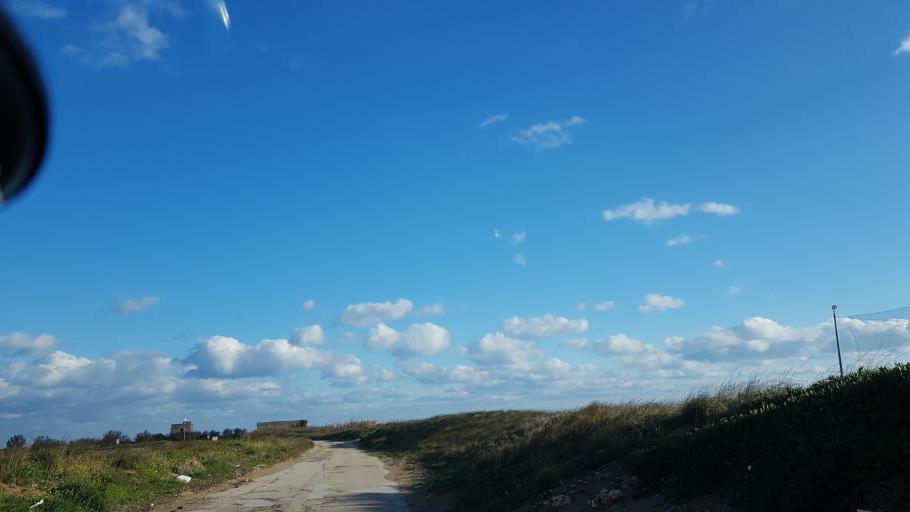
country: IT
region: Apulia
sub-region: Provincia di Brindisi
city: Materdomini
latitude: 40.6809
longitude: 17.9343
